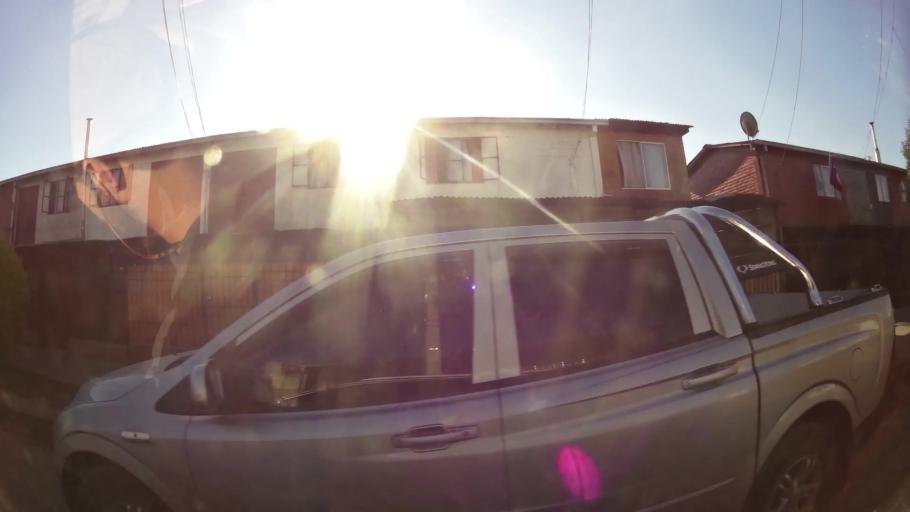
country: CL
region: Santiago Metropolitan
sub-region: Provincia de Talagante
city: Penaflor
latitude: -33.6029
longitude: -70.8611
